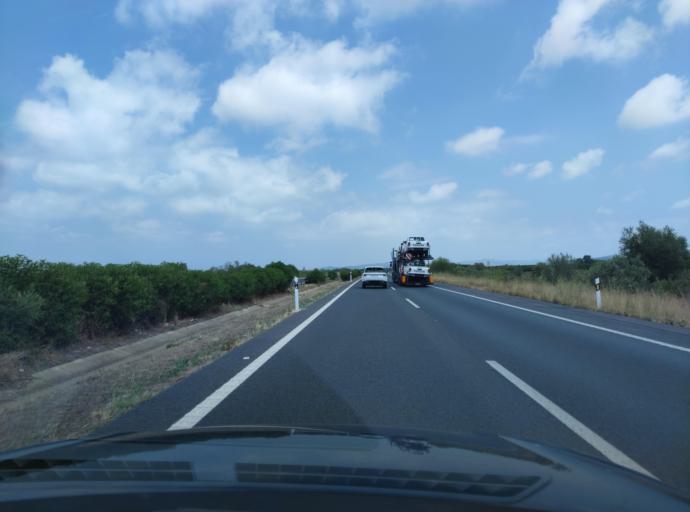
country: ES
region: Catalonia
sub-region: Provincia de Tarragona
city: Alcanar
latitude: 40.5144
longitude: 0.4155
